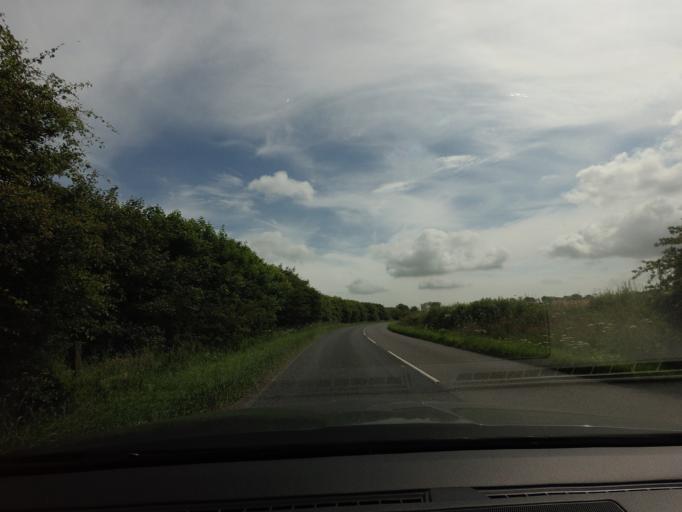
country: GB
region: Scotland
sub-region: Aberdeenshire
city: Mintlaw
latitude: 57.5255
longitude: -1.9775
